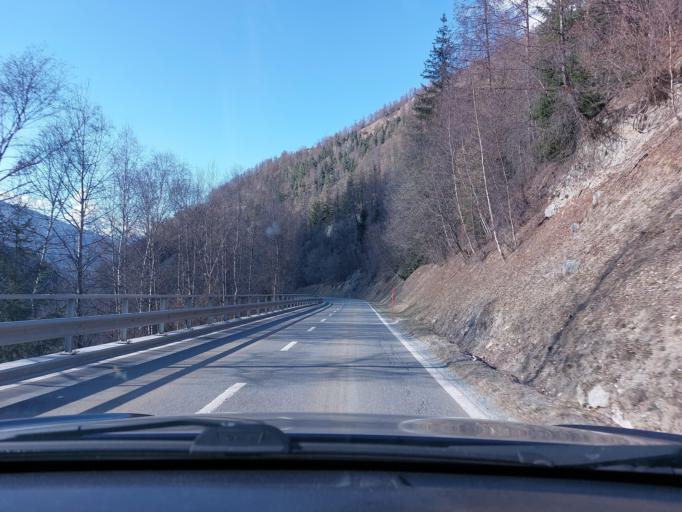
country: CH
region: Valais
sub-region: Herens District
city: Evolene
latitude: 46.1428
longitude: 7.4648
